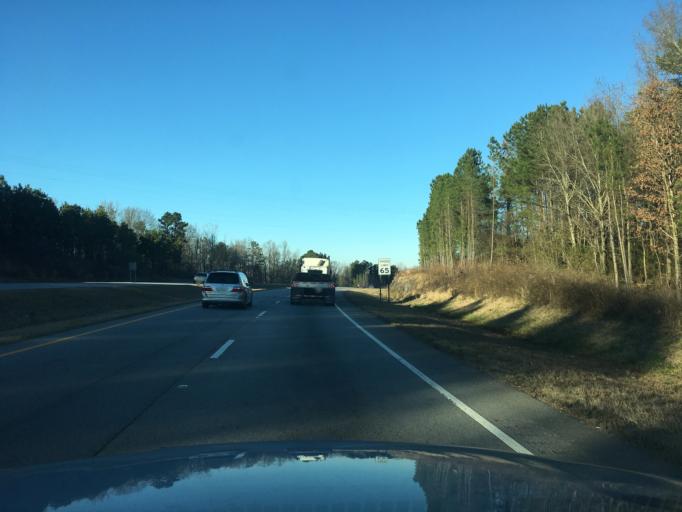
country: US
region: Georgia
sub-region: Carroll County
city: Carrollton
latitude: 33.4613
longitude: -85.1238
